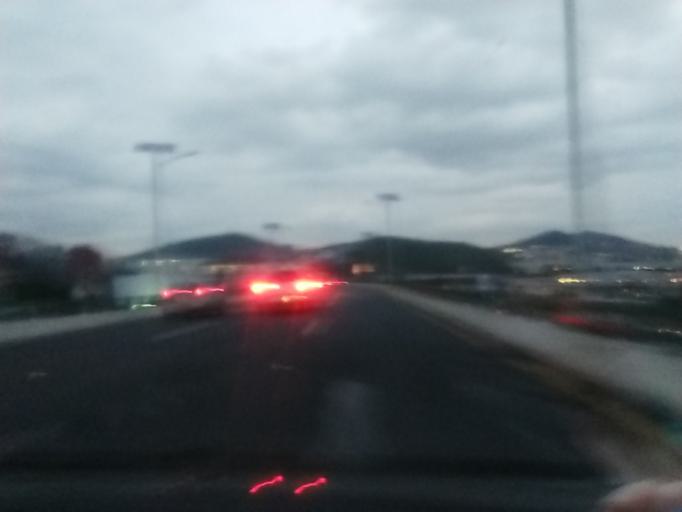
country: MX
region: Mexico
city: Tlalnepantla
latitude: 19.5624
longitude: -99.2064
